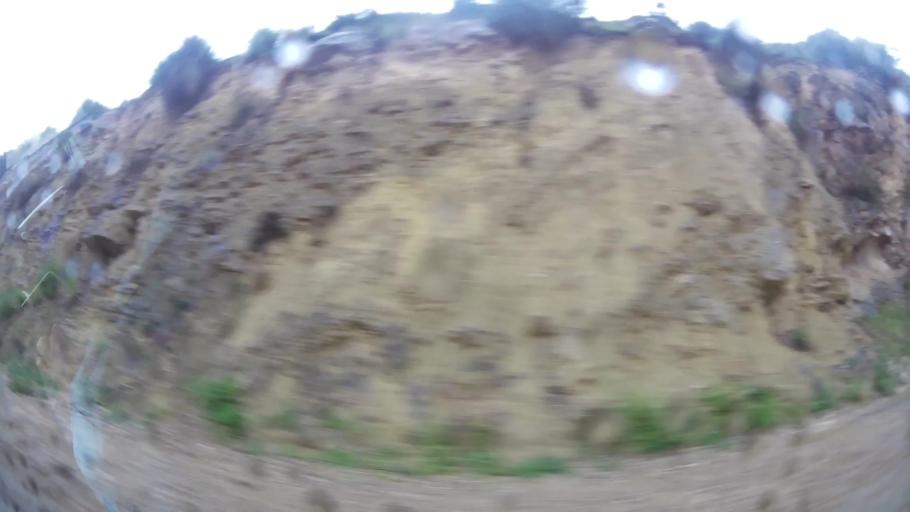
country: MA
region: Taza-Al Hoceima-Taounate
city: Tirhanimine
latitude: 35.2307
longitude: -3.9643
